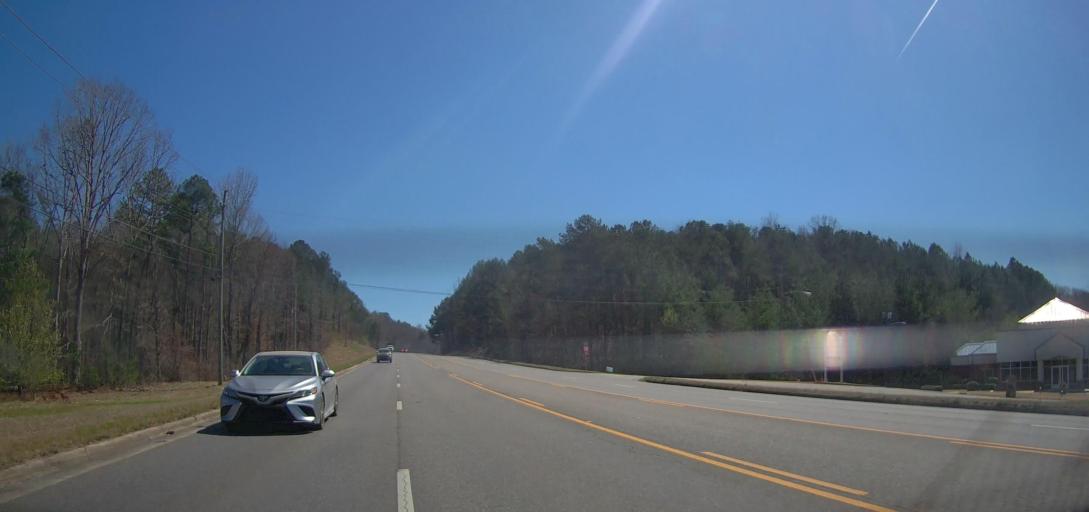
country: US
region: Alabama
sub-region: Etowah County
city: Rainbow City
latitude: 33.9516
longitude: -86.0353
